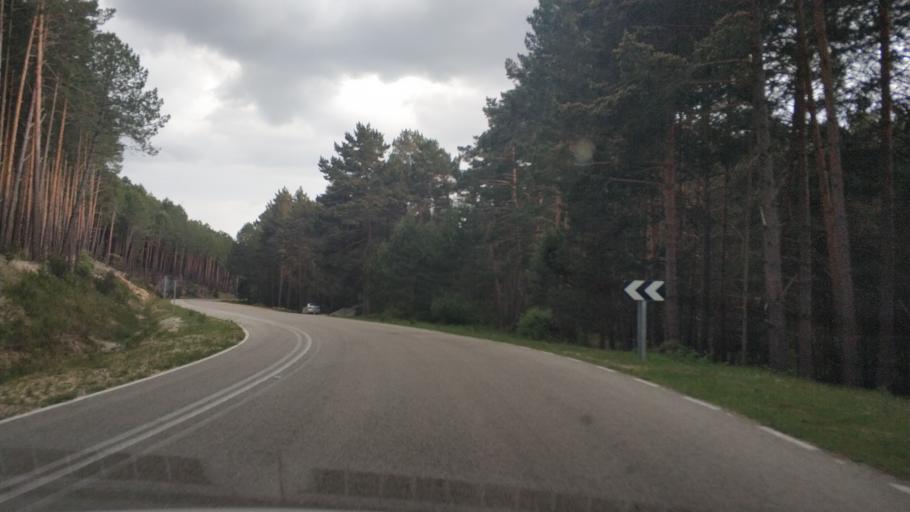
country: ES
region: Castille and Leon
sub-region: Provincia de Soria
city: San Leonardo de Yague
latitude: 41.8447
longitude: -3.0682
